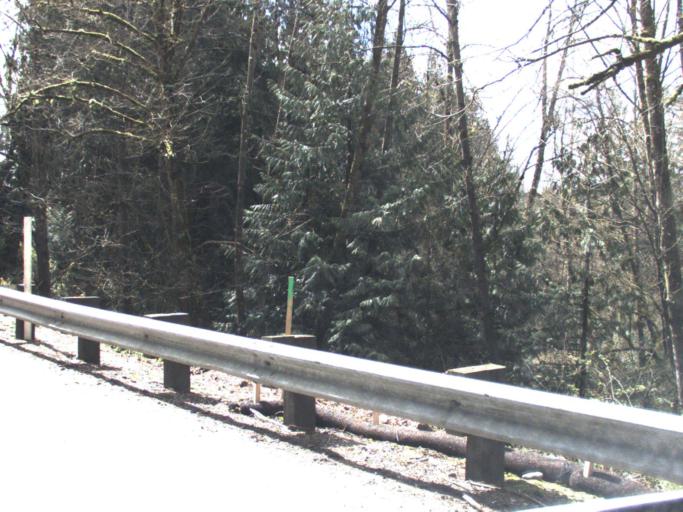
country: US
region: Washington
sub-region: Pierce County
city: Bonney Lake
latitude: 47.2335
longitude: -122.1057
